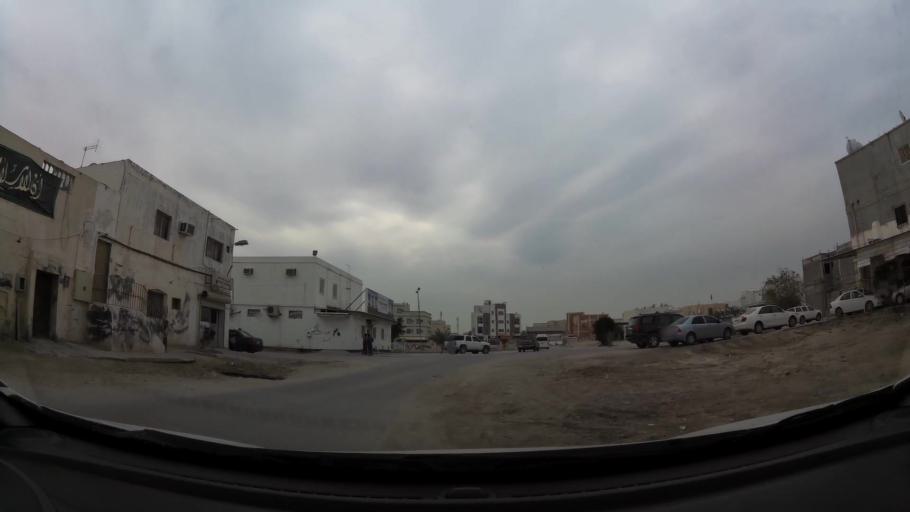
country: BH
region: Northern
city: Sitrah
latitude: 26.1447
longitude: 50.6101
